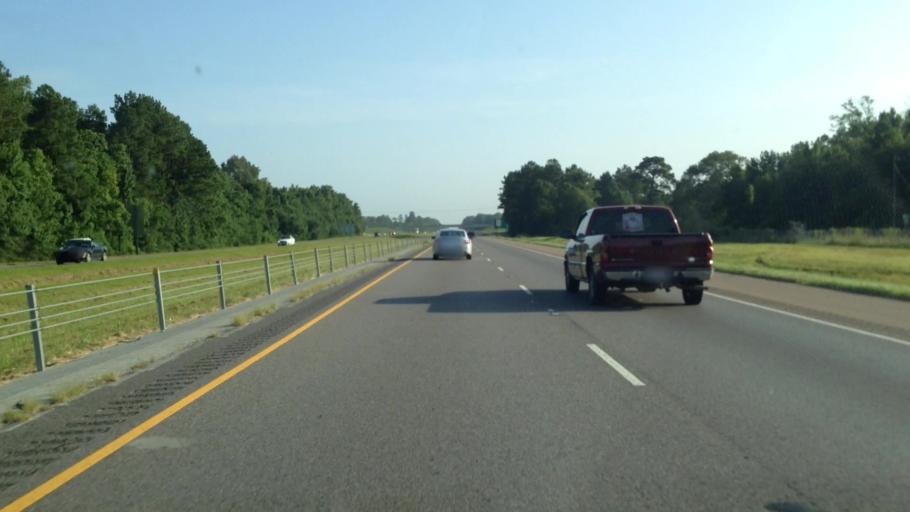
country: US
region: Louisiana
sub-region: Tangipahoa Parish
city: Natalbany
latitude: 30.5110
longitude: -90.5036
